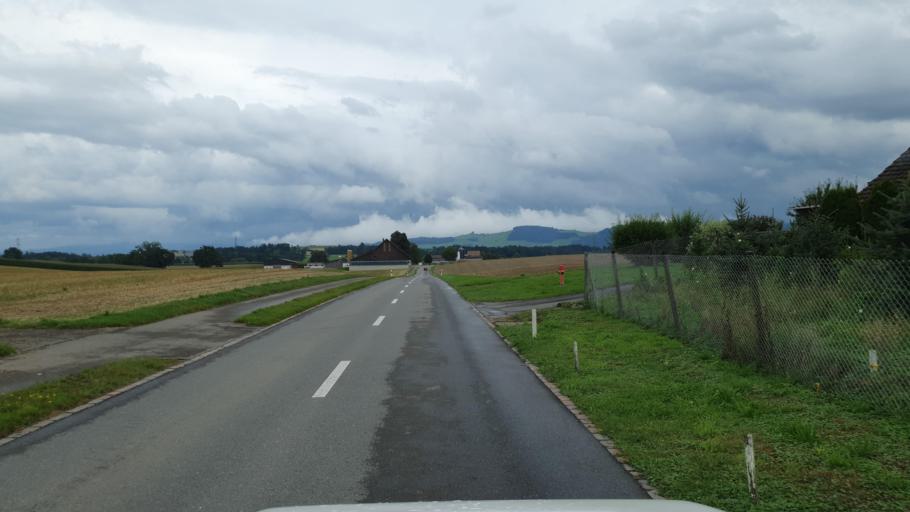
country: CH
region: Lucerne
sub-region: Hochdorf District
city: Ballwil
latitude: 47.1452
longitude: 8.3346
